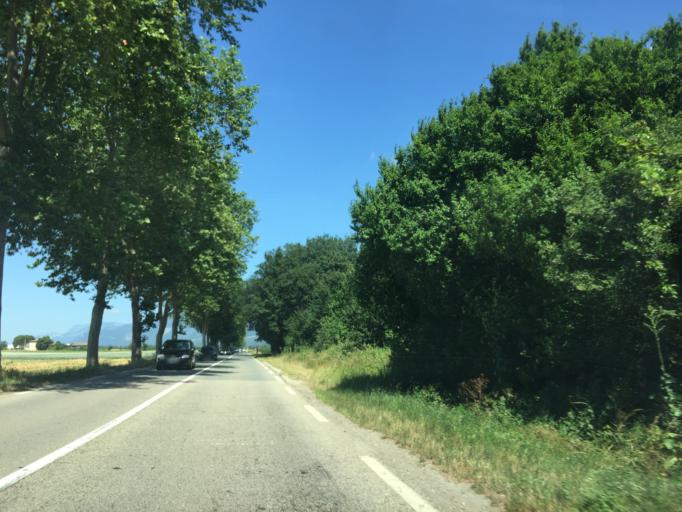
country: FR
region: Rhone-Alpes
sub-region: Departement de l'Isere
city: Saint-Lattier
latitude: 45.0620
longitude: 5.2151
